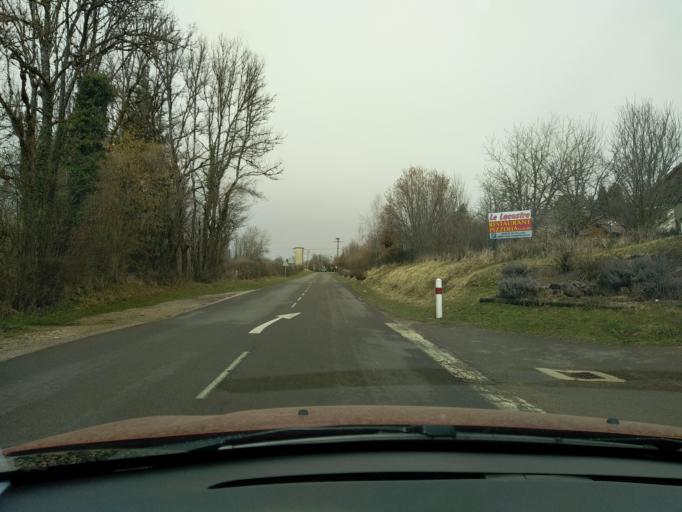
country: FR
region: Franche-Comte
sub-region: Departement du Jura
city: Clairvaux-les-Lacs
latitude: 46.6484
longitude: 5.7754
